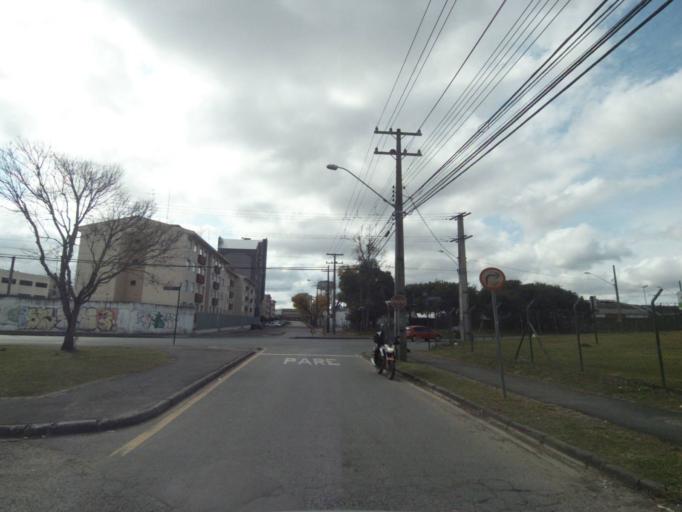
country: BR
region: Parana
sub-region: Curitiba
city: Curitiba
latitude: -25.4679
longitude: -49.2575
